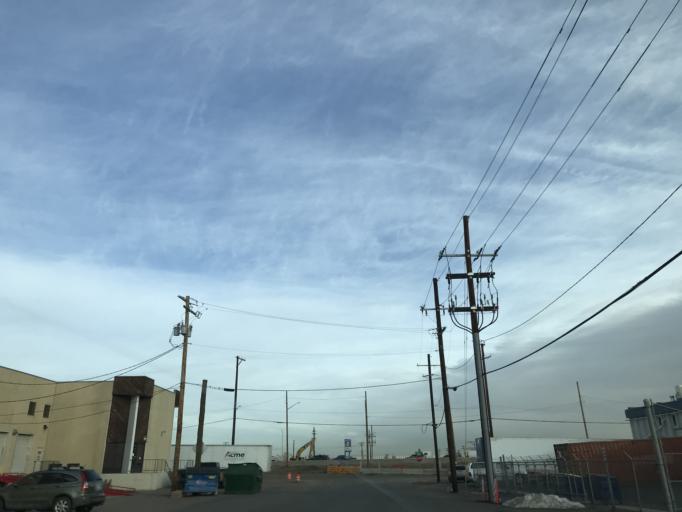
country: US
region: Colorado
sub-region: Adams County
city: Commerce City
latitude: 39.7779
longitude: -104.9258
